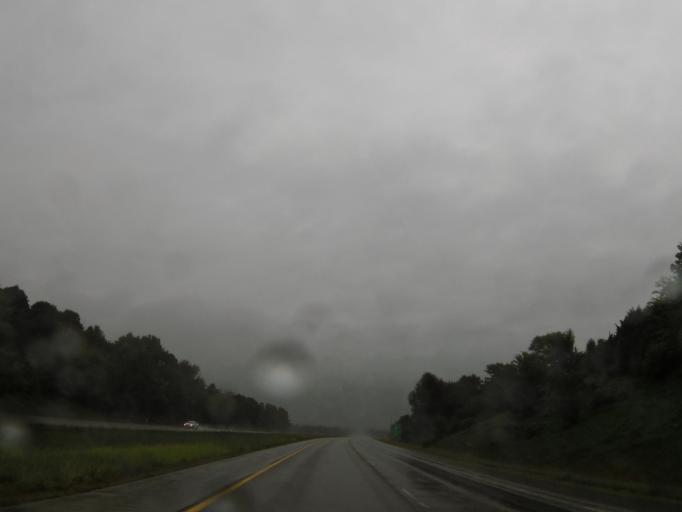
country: US
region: Illinois
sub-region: Johnson County
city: Vienna
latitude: 37.4393
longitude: -88.8853
